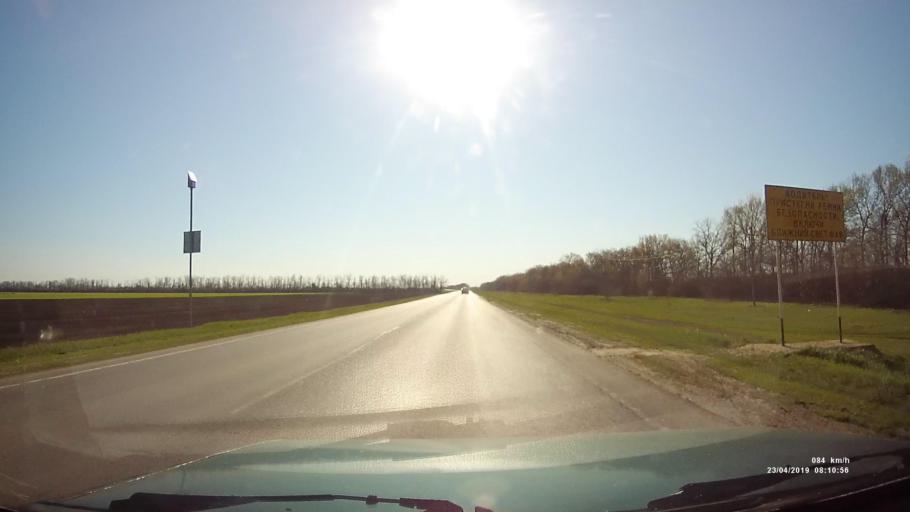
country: RU
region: Rostov
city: Yegorlykskaya
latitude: 46.5553
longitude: 40.6894
